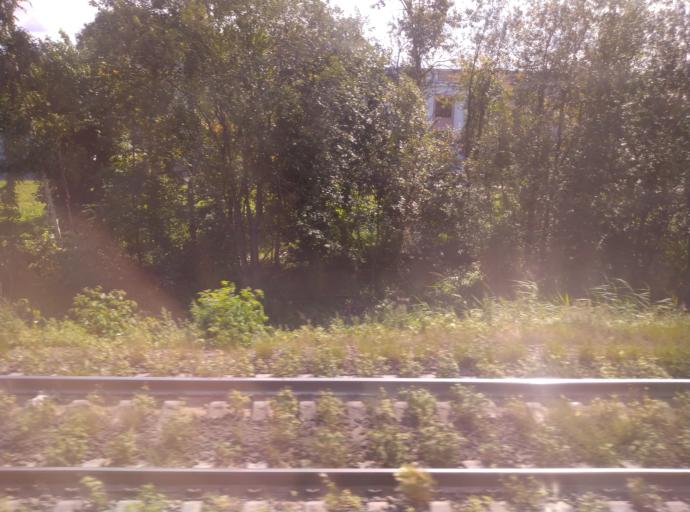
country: RU
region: St.-Petersburg
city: Centralniy
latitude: 59.9074
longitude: 30.3843
